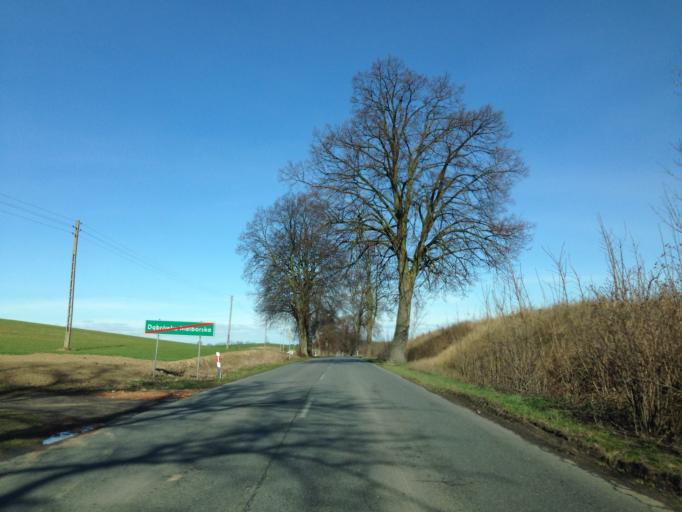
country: PL
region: Pomeranian Voivodeship
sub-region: Powiat malborski
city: Malbork
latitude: 53.9956
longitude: 19.1013
